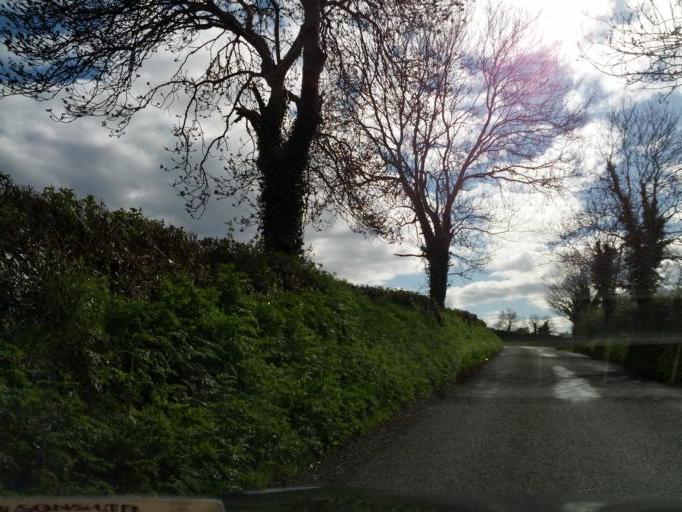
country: IE
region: Leinster
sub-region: Kildare
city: Kilcock
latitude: 53.4950
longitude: -6.6862
